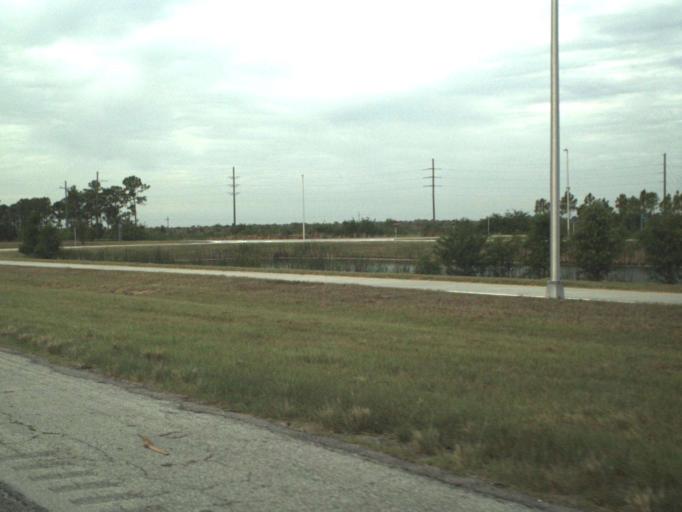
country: US
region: Florida
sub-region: Saint Lucie County
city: Port Saint Lucie
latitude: 27.1881
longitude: -80.3995
